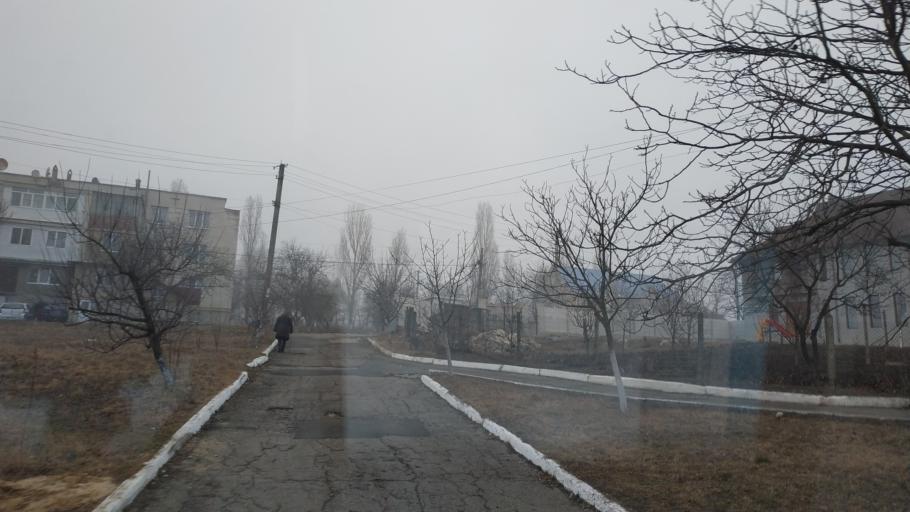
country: MD
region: Laloveni
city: Ialoveni
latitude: 46.9604
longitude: 28.7097
